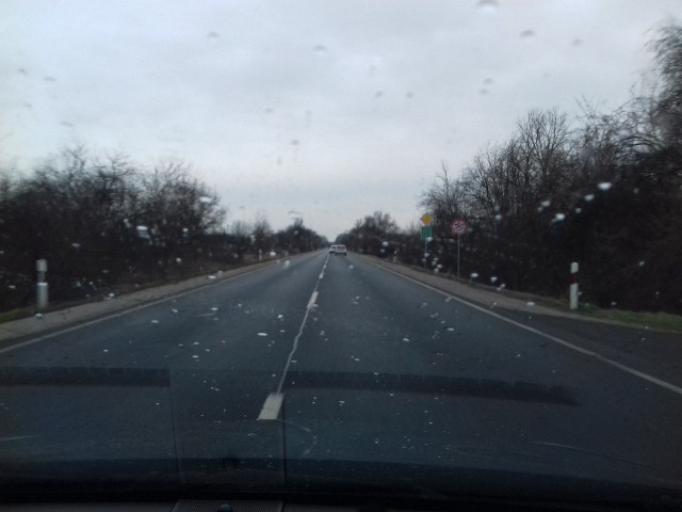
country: HU
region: Szabolcs-Szatmar-Bereg
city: Ujfeherto
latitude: 47.8514
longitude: 21.7040
